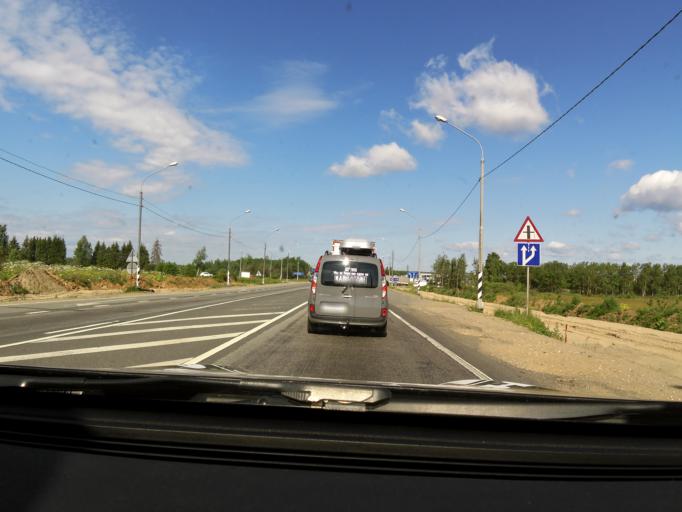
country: RU
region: Tverskaya
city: Tver
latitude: 56.7878
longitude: 35.9177
